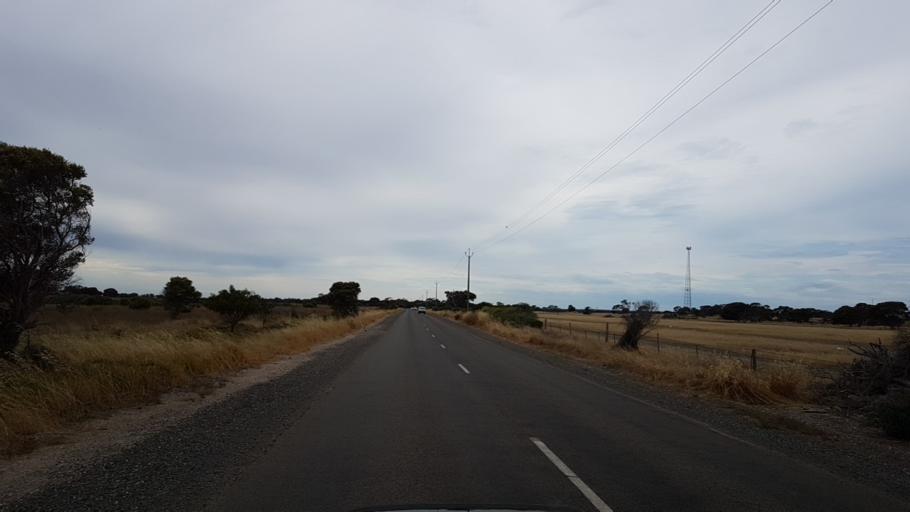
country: AU
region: South Australia
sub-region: Yorke Peninsula
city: Port Victoria
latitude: -34.9187
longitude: 137.0680
